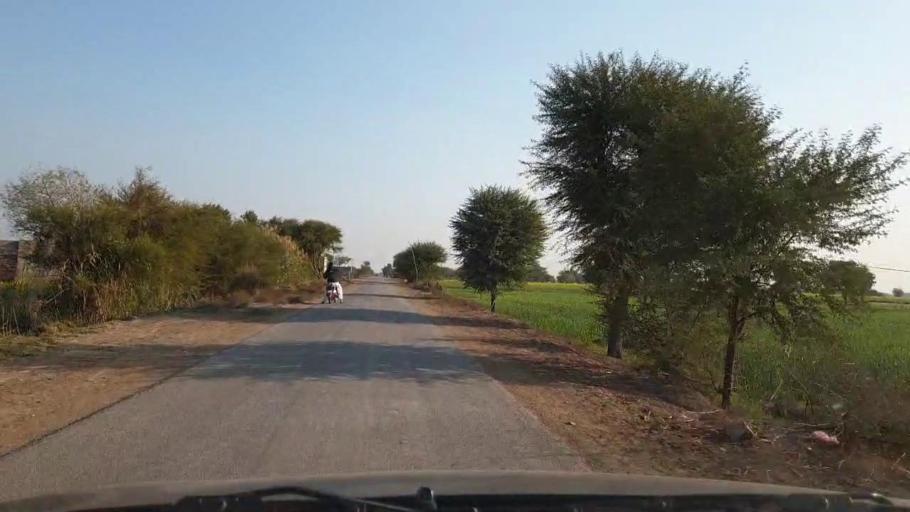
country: PK
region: Sindh
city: Jhol
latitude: 25.9530
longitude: 68.9001
